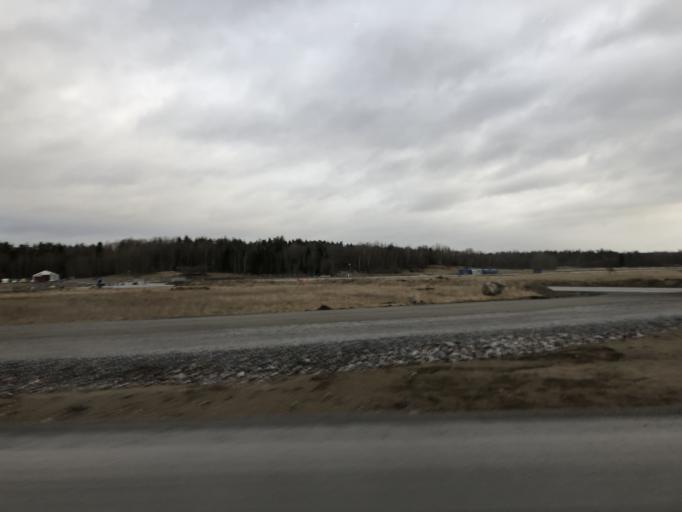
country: SE
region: Stockholm
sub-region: Jarfalla Kommun
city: Jakobsberg
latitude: 59.4127
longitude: 17.8827
